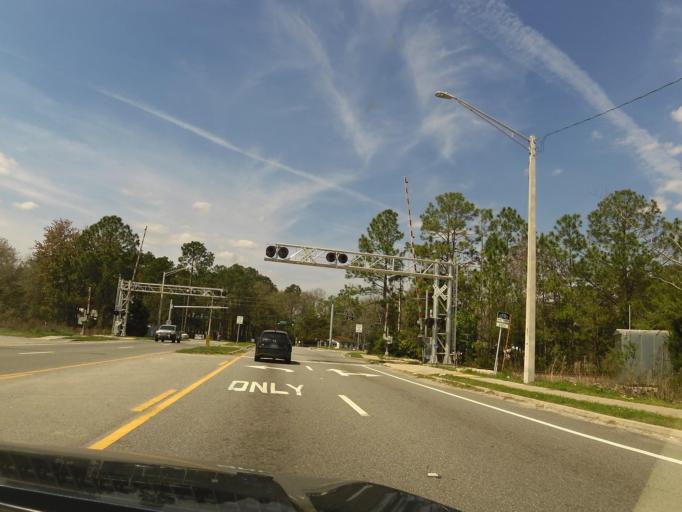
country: US
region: Florida
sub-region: Duval County
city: Jacksonville
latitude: 30.3194
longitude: -81.7929
